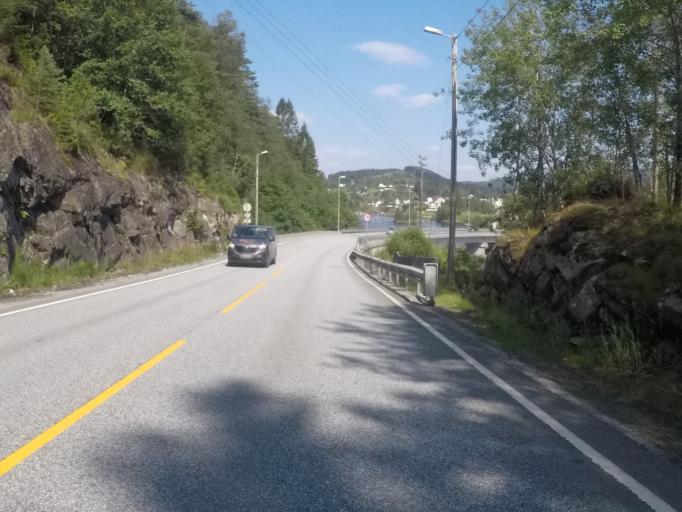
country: NO
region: Hordaland
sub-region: Bergen
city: Hylkje
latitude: 60.6022
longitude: 5.3974
